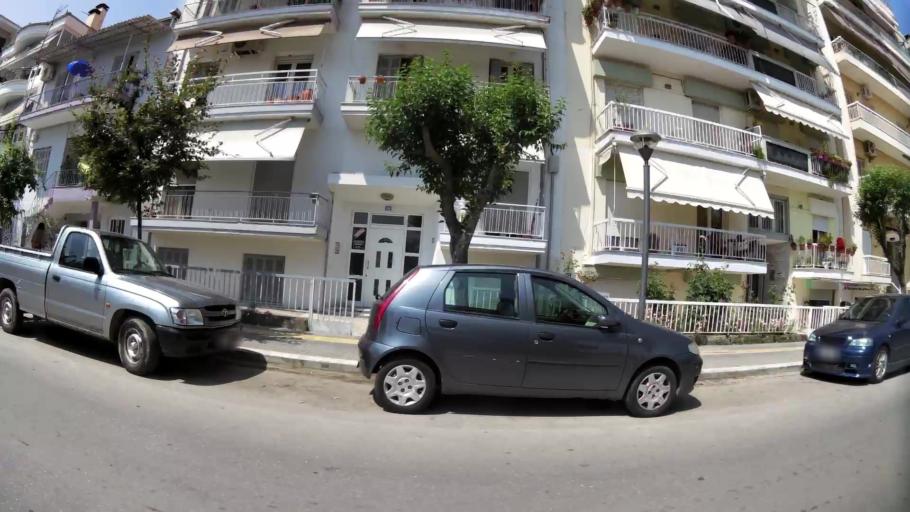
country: GR
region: Central Macedonia
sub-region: Nomos Imathias
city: Veroia
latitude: 40.5282
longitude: 22.2069
